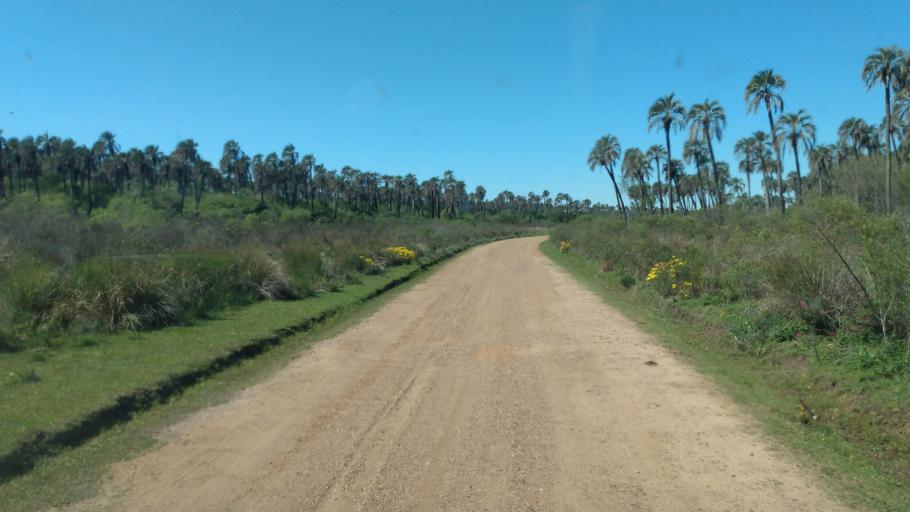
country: AR
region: Entre Rios
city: Ubajay
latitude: -31.8794
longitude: -58.2359
